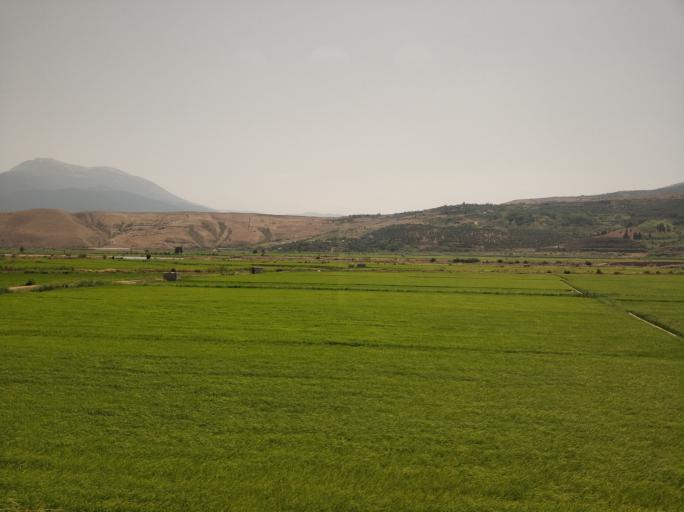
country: IR
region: Gilan
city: Pa'in-e Bazar-e Rudbar
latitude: 36.8789
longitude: 49.4964
